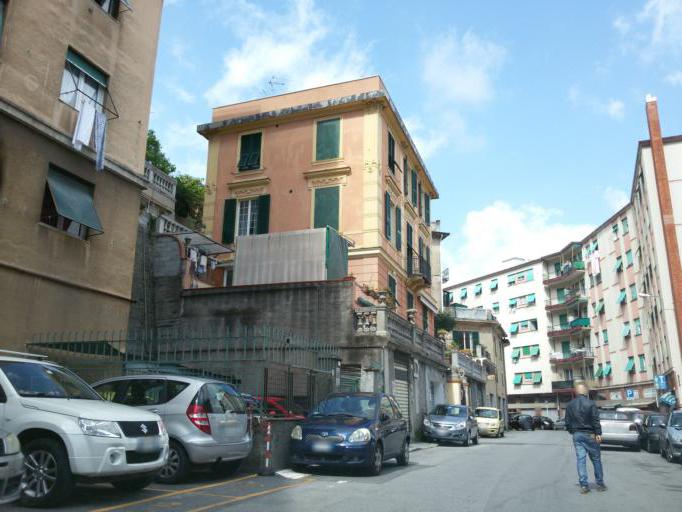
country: IT
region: Liguria
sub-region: Provincia di Genova
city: Genoa
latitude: 44.4222
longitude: 8.9447
